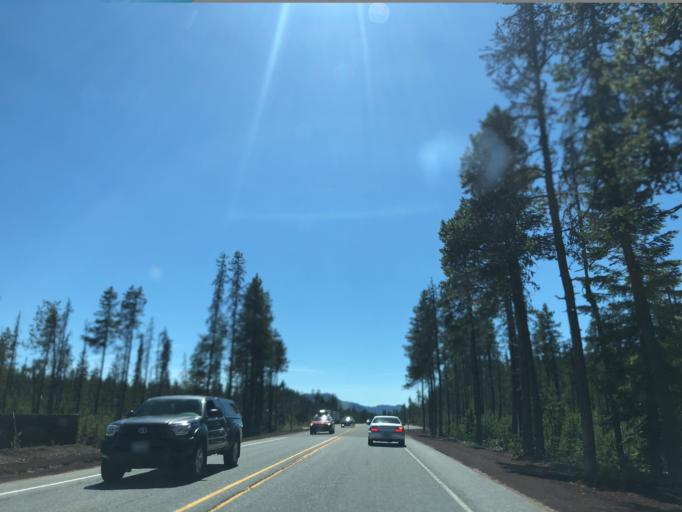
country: US
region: Oregon
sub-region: Deschutes County
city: Sisters
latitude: 44.4360
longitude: -121.9445
